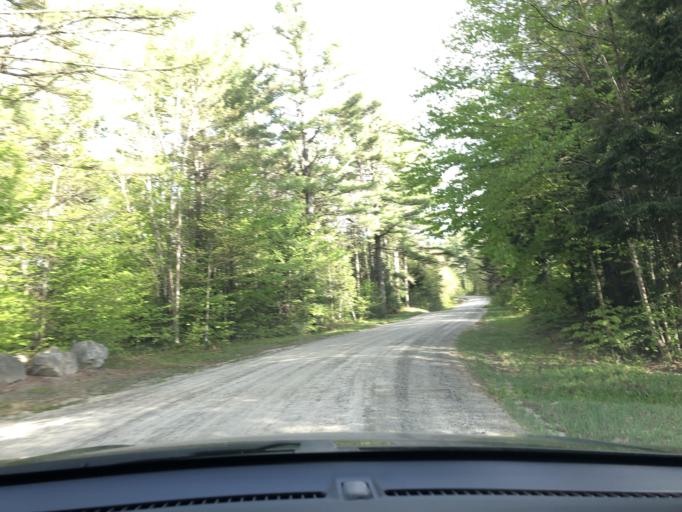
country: US
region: New Hampshire
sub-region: Merrimack County
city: New London
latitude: 43.4040
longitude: -72.0144
